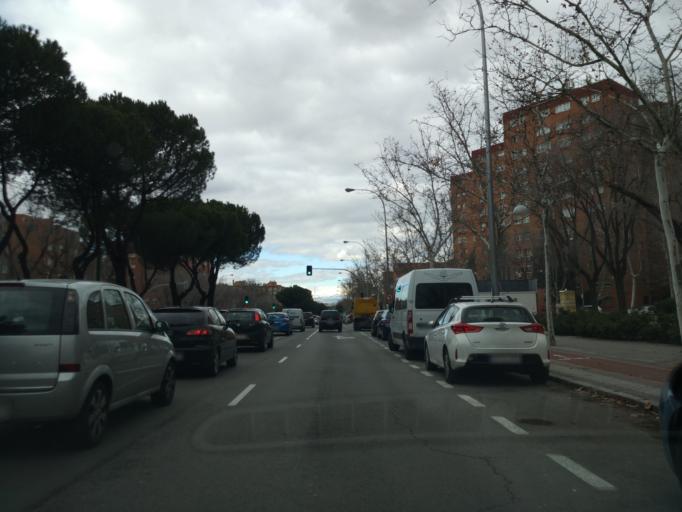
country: ES
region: Madrid
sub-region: Provincia de Madrid
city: San Blas
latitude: 40.4216
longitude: -3.6261
